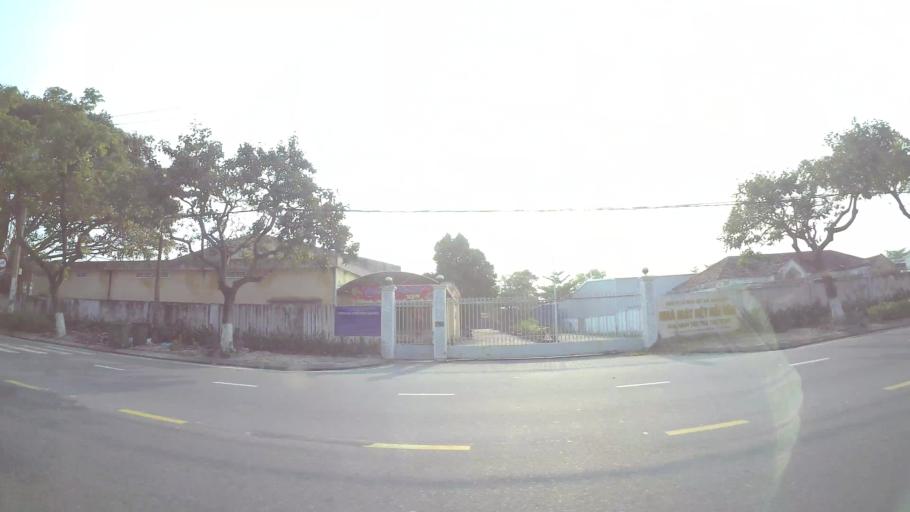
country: VN
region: Da Nang
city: Cam Le
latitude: 16.0216
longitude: 108.2026
